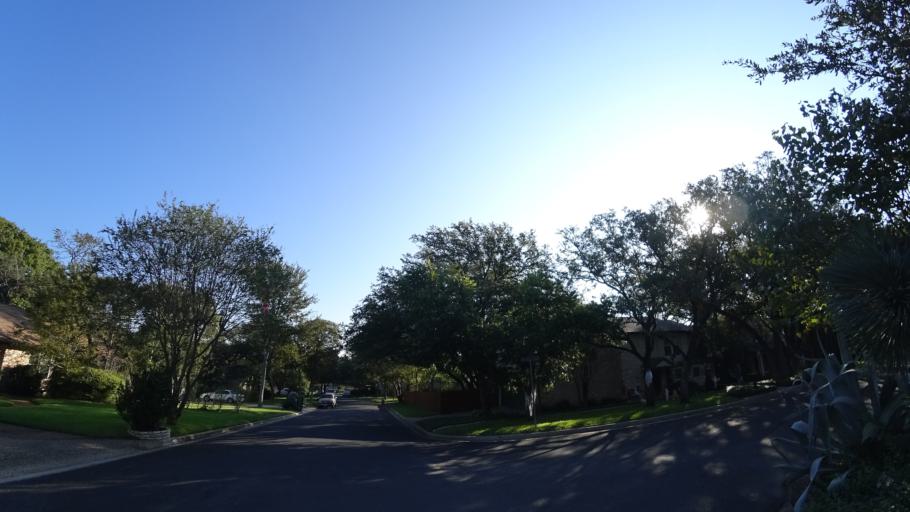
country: US
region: Texas
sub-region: Travis County
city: Rollingwood
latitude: 30.2642
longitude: -97.8053
